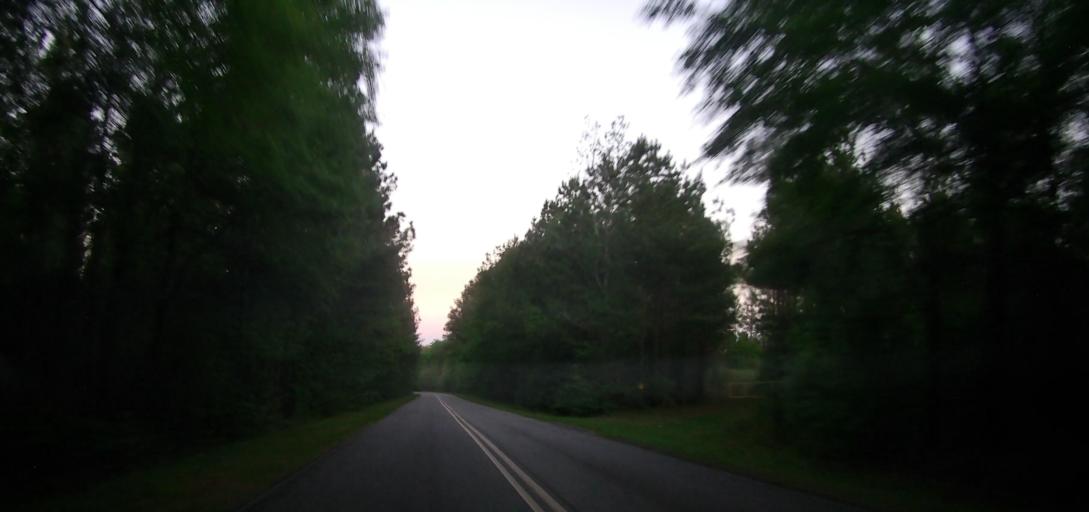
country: US
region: Georgia
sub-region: Marion County
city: Buena Vista
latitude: 32.2548
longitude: -84.5862
